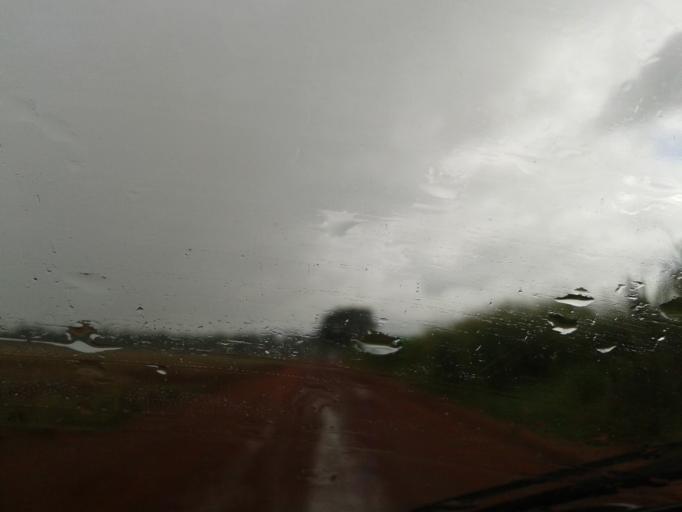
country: BR
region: Minas Gerais
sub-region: Santa Vitoria
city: Santa Vitoria
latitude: -18.6550
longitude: -49.9119
